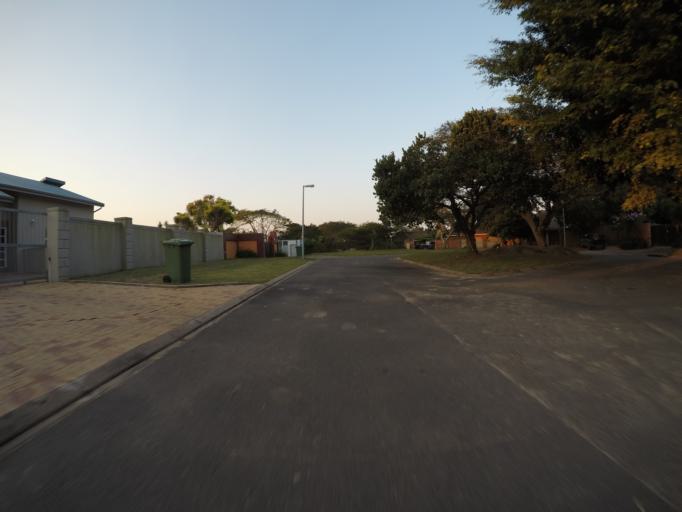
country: ZA
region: KwaZulu-Natal
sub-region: uThungulu District Municipality
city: Richards Bay
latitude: -28.7675
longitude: 32.1254
